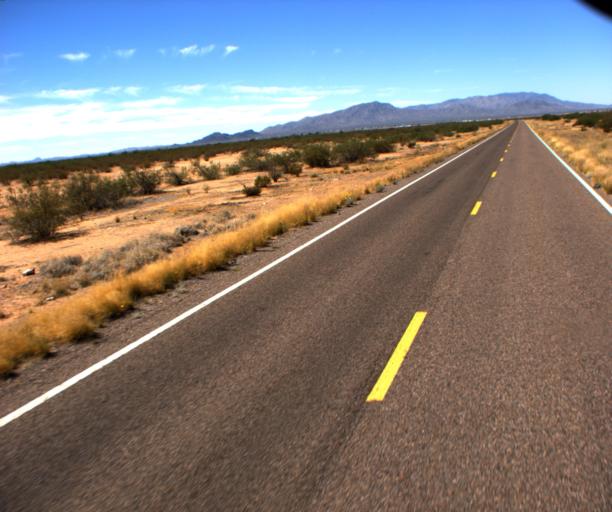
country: US
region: Arizona
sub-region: Yavapai County
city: Congress
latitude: 33.9966
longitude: -113.1261
